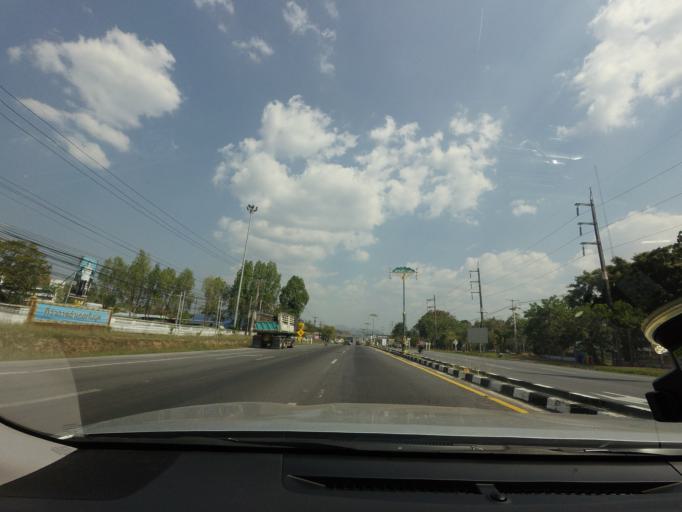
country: TH
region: Phangnga
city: Thap Put
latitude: 8.5154
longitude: 98.6392
